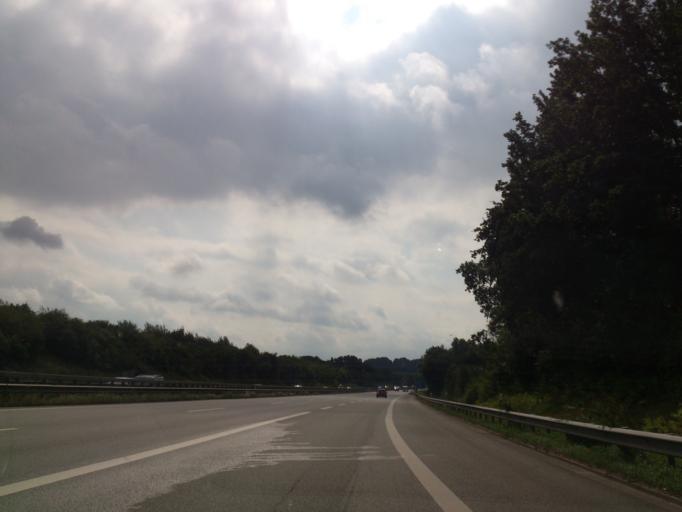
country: DE
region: Lower Saxony
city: Seevetal
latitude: 53.4227
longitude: 9.9673
